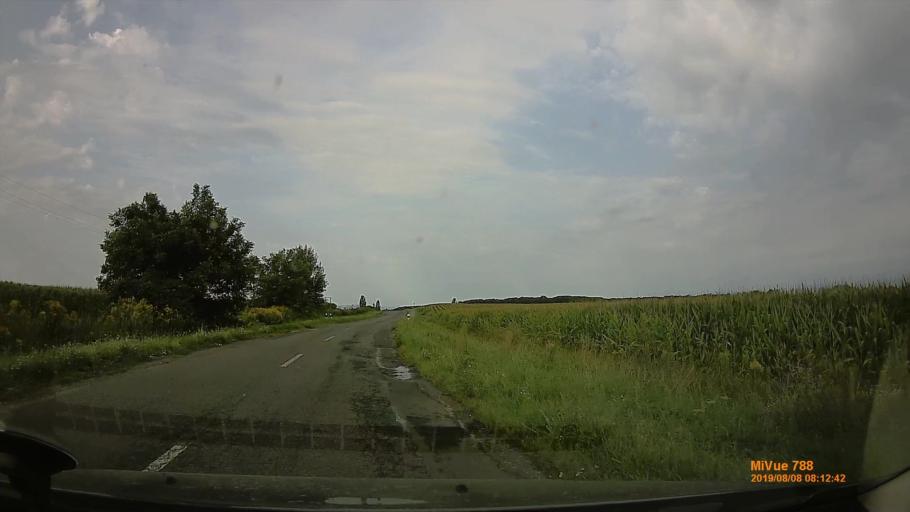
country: HU
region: Zala
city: Murakeresztur
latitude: 46.4118
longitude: 16.8687
